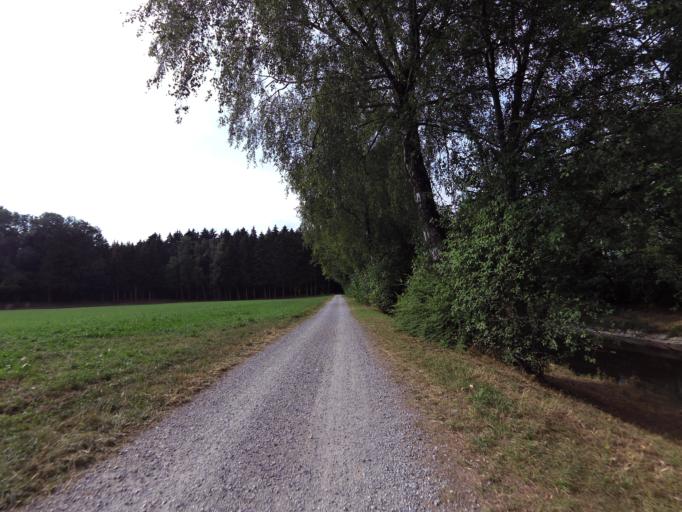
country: CH
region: Zurich
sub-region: Bezirk Buelach
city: Glattbrugg
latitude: 47.4405
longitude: 8.5540
